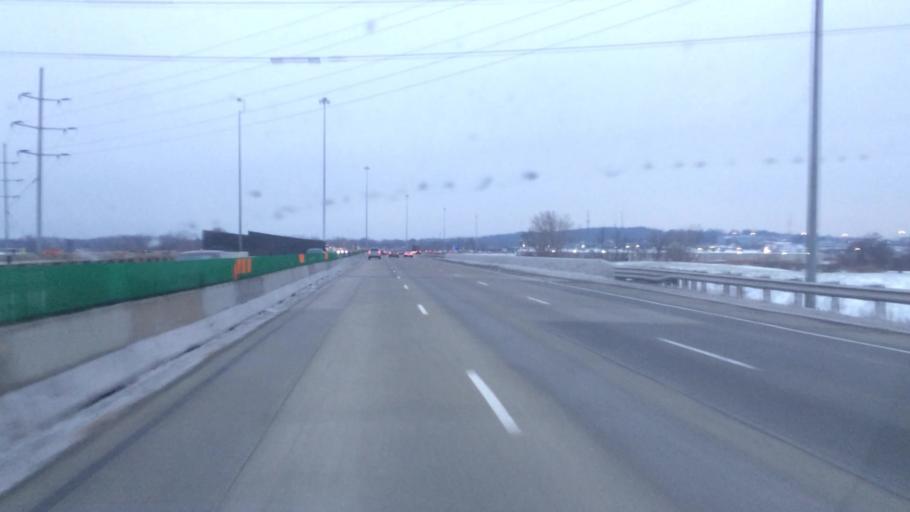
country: US
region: Ohio
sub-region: Cuyahoga County
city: Bedford Heights
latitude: 41.4171
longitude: -81.5082
